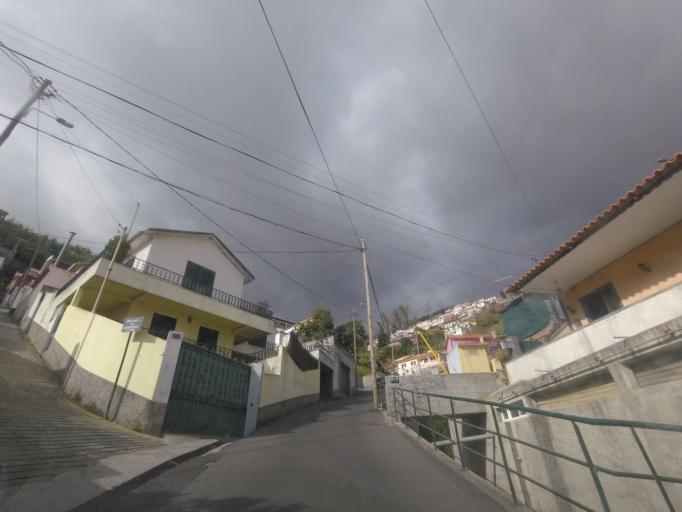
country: PT
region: Madeira
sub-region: Funchal
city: Nossa Senhora do Monte
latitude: 32.6741
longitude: -16.9313
